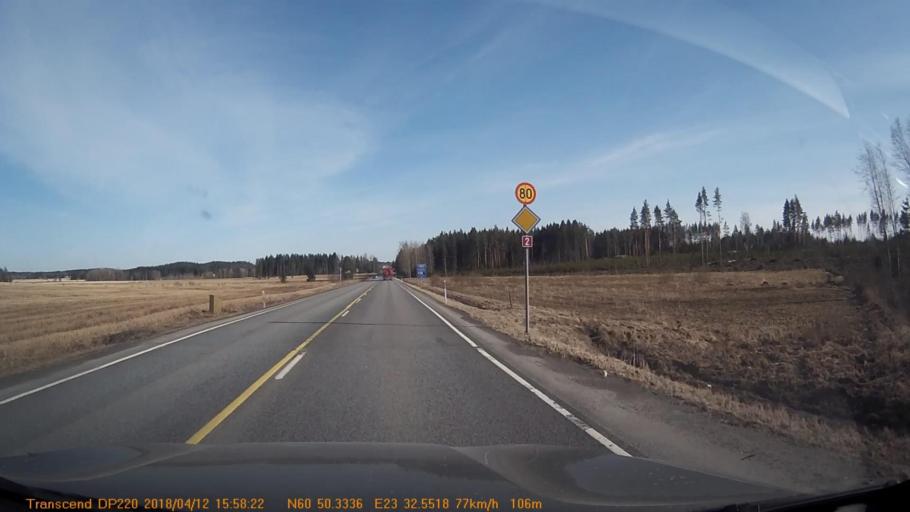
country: FI
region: Haeme
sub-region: Forssa
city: Jokioinen
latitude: 60.8383
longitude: 23.5439
